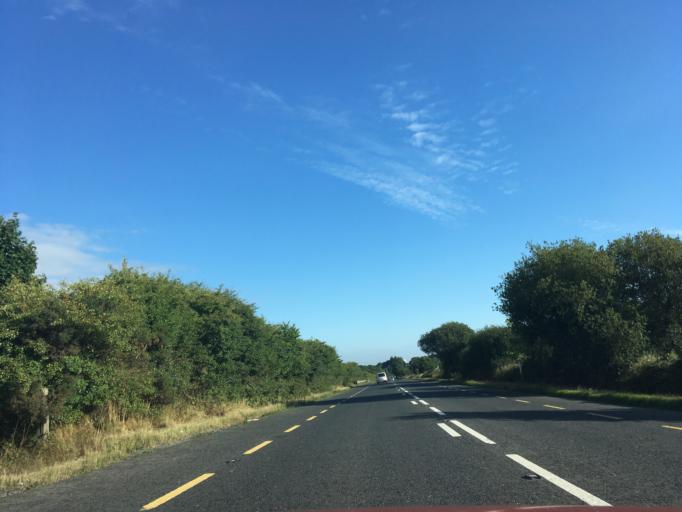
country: IE
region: Munster
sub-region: Waterford
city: Waterford
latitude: 52.3205
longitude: -7.0542
